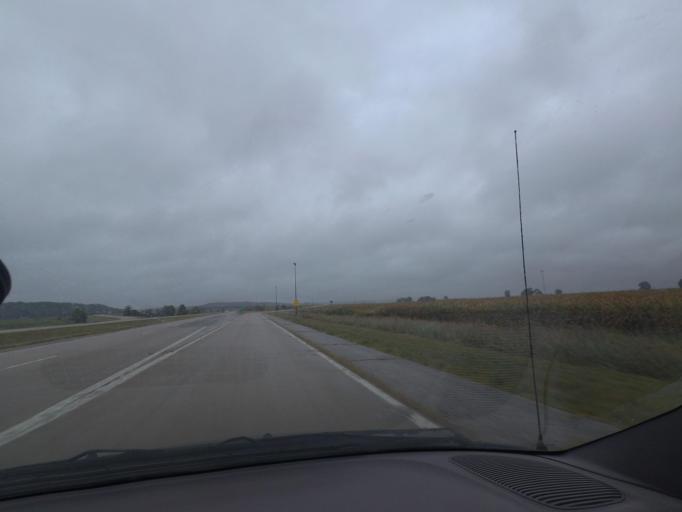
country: US
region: Illinois
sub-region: Adams County
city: Payson
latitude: 39.7193
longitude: -91.2006
